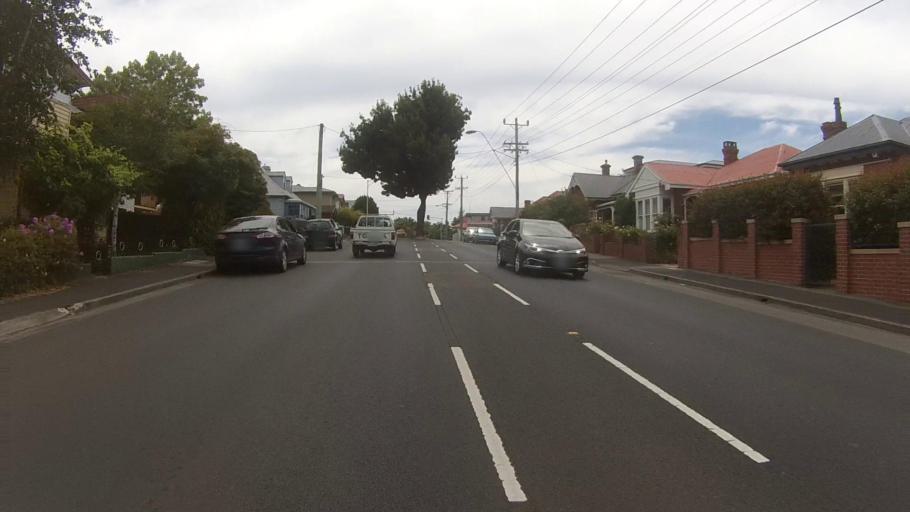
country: AU
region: Tasmania
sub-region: Hobart
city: Sandy Bay
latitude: -42.8967
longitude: 147.3236
